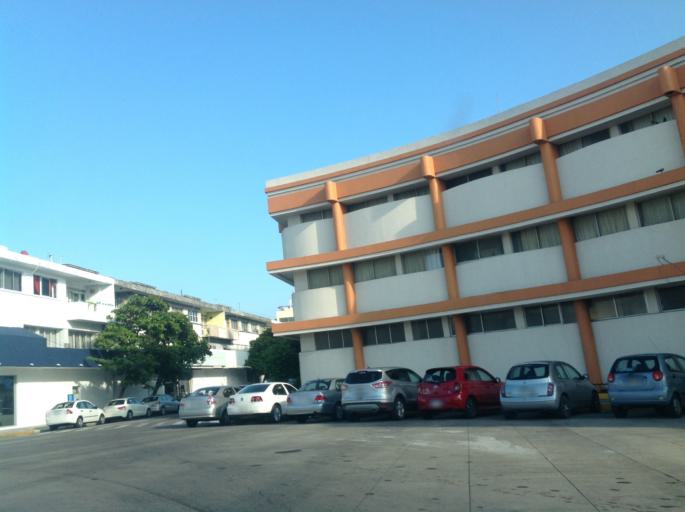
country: MX
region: Veracruz
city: Veracruz
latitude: 19.2002
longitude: -96.1344
